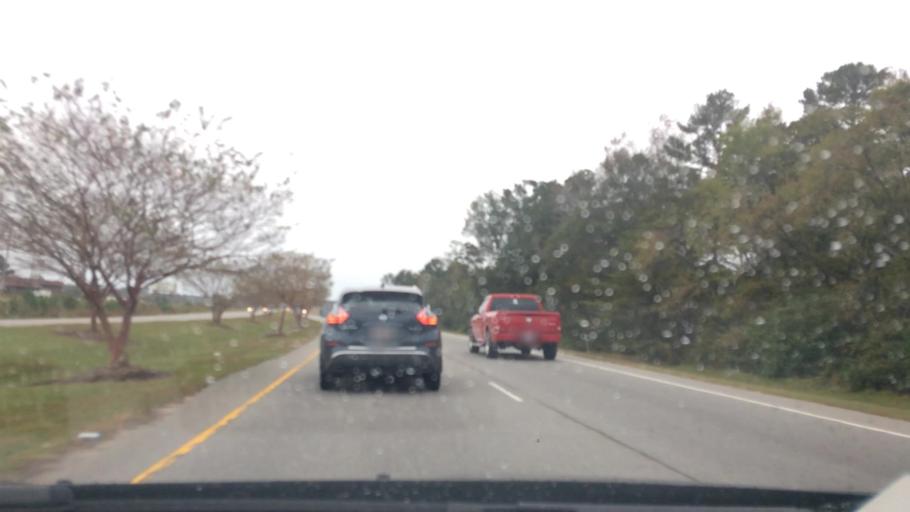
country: US
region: North Carolina
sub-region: Pitt County
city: Ayden
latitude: 35.4738
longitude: -77.4356
